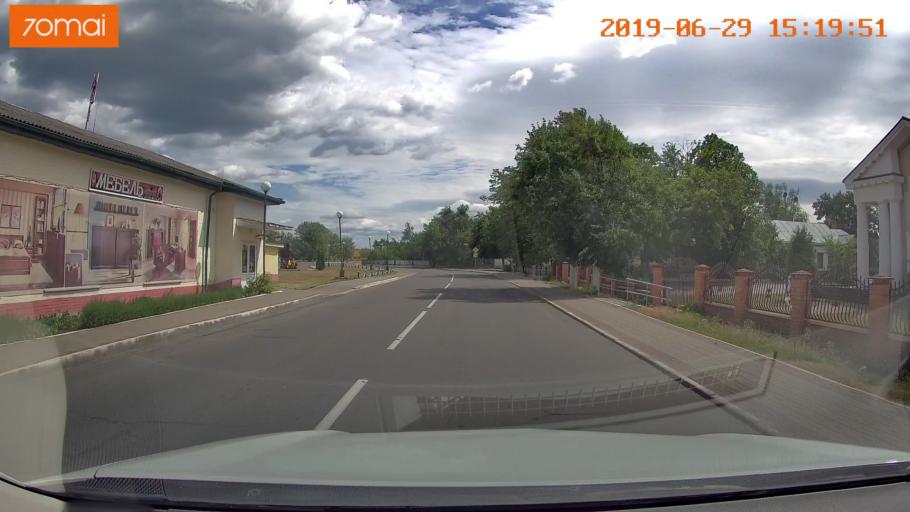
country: BY
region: Brest
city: Mikashevichy
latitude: 52.2175
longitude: 27.4704
